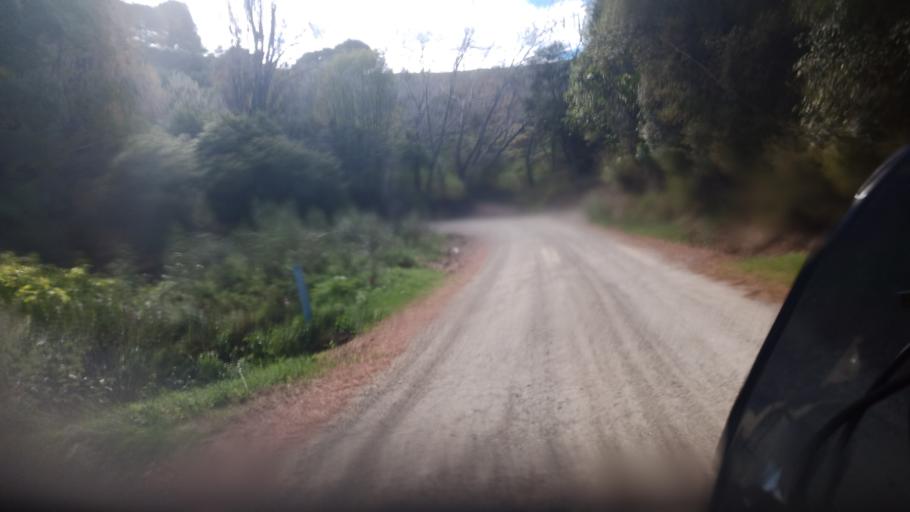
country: NZ
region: Gisborne
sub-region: Gisborne District
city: Gisborne
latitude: -38.4104
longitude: 177.6873
